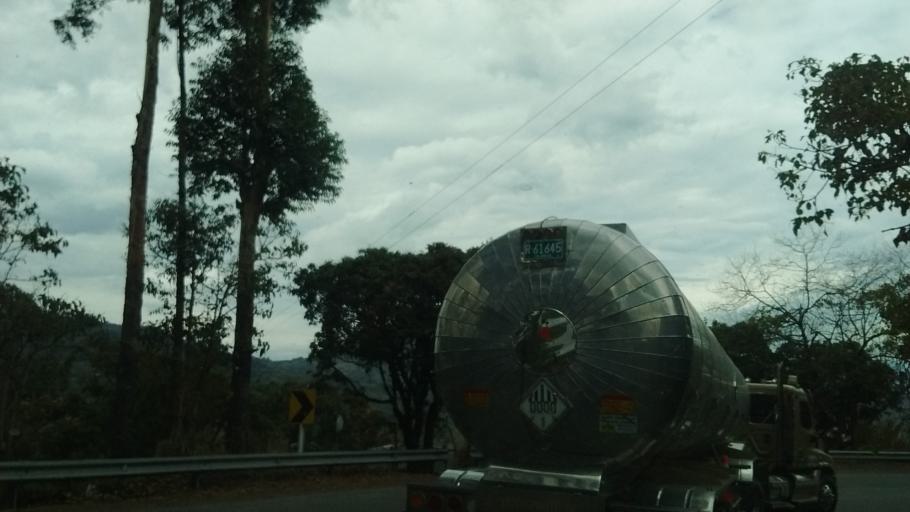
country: CO
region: Cauca
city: Rosas
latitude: 2.2869
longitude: -76.7070
